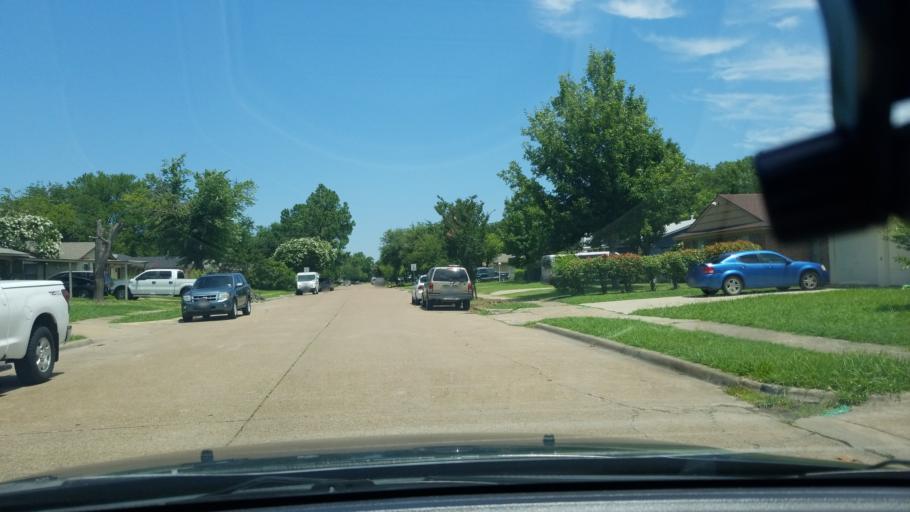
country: US
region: Texas
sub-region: Dallas County
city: Mesquite
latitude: 32.8043
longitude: -96.6573
